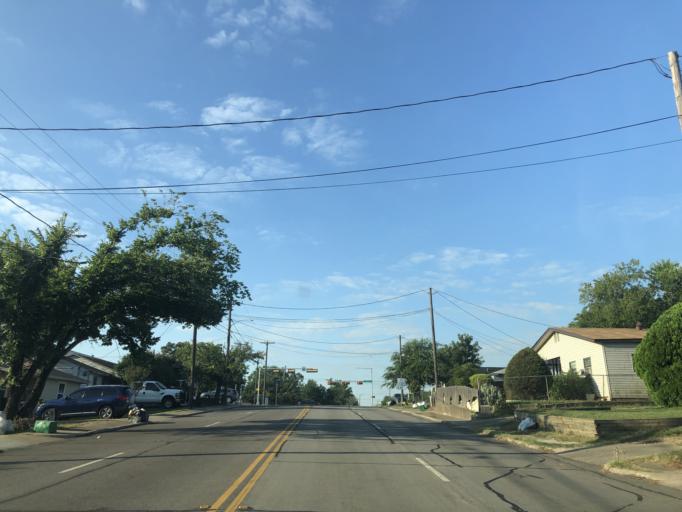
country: US
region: Texas
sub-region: Dallas County
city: Grand Prairie
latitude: 32.7458
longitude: -97.0288
